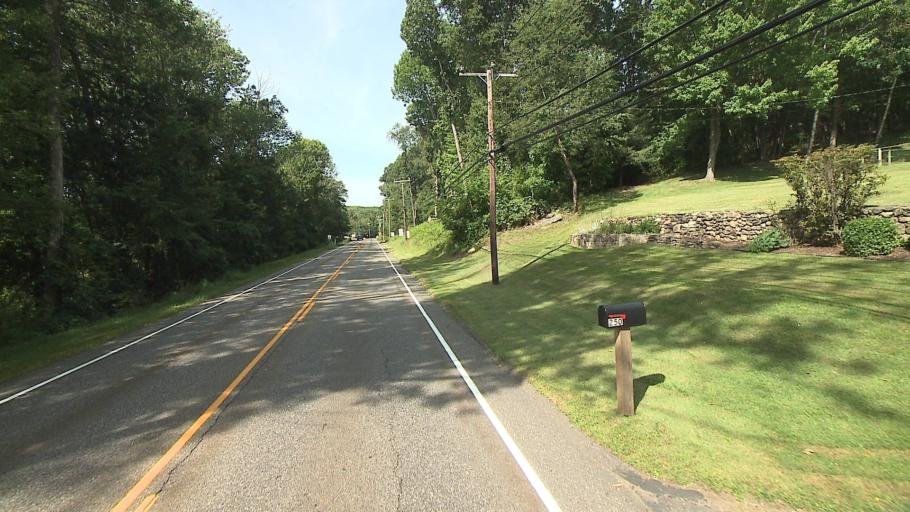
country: US
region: Connecticut
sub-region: Litchfield County
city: Northwest Harwinton
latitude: 41.7678
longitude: -73.0816
